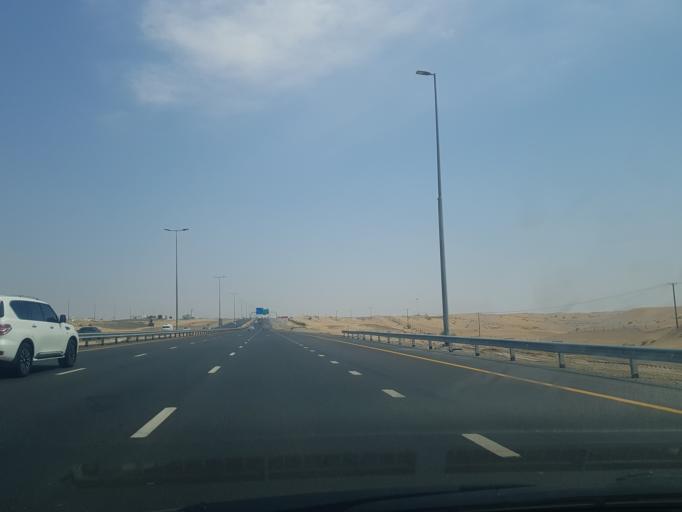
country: AE
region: Ash Shariqah
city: Sharjah
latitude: 25.2315
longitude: 55.5837
